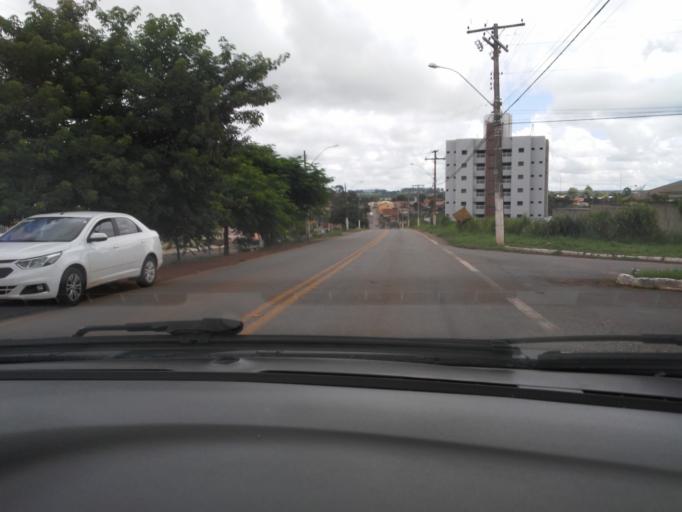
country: BR
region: Goias
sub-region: Ipameri
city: Ipameri
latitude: -17.7357
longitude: -48.1619
